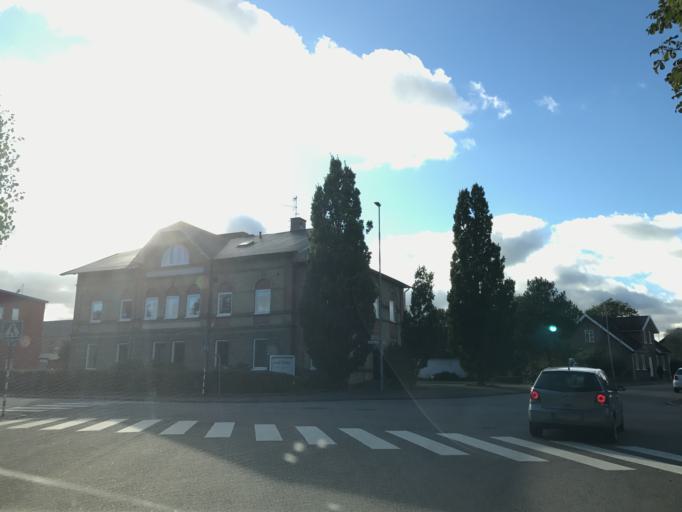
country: SE
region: Skane
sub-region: Klippans Kommun
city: Klippan
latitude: 56.1335
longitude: 13.1291
